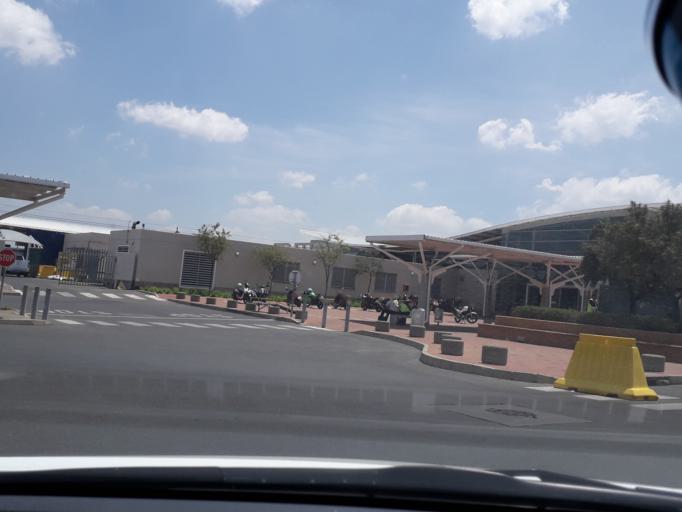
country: ZA
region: Gauteng
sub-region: City of Johannesburg Metropolitan Municipality
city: Midrand
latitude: -25.9959
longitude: 28.1363
